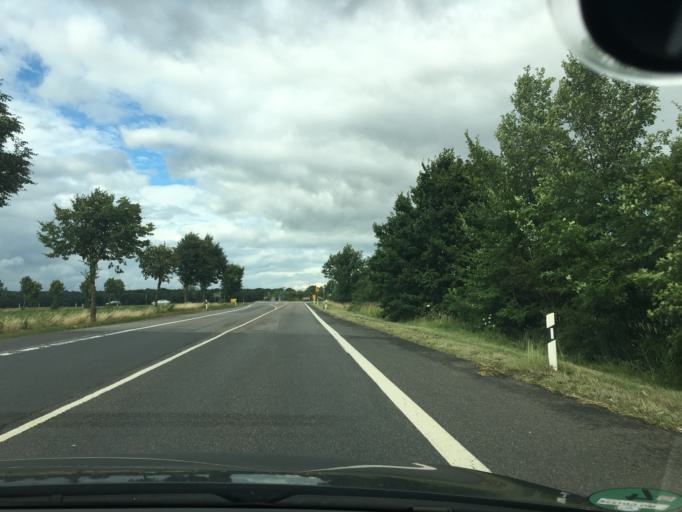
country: DE
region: North Rhine-Westphalia
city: Zulpich
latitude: 50.7190
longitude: 6.6873
